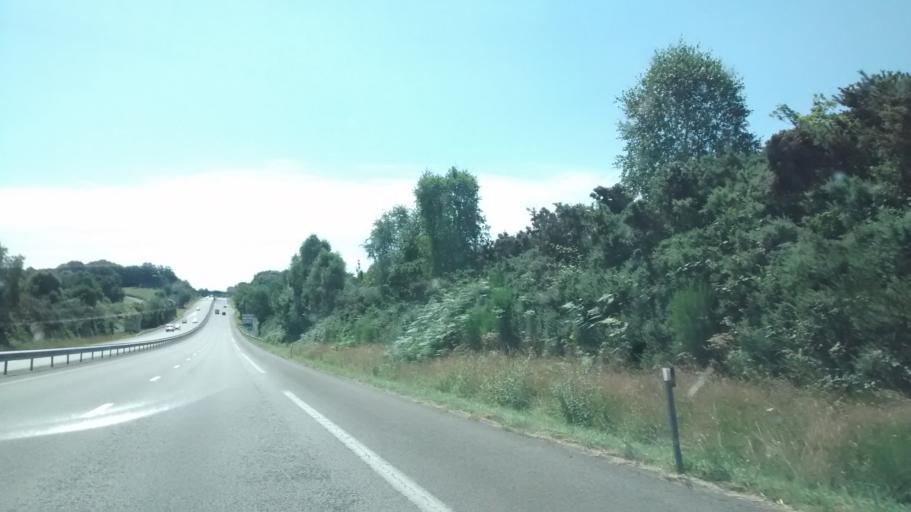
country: FR
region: Brittany
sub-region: Departement du Morbihan
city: Augan
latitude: 47.9339
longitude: -2.2520
